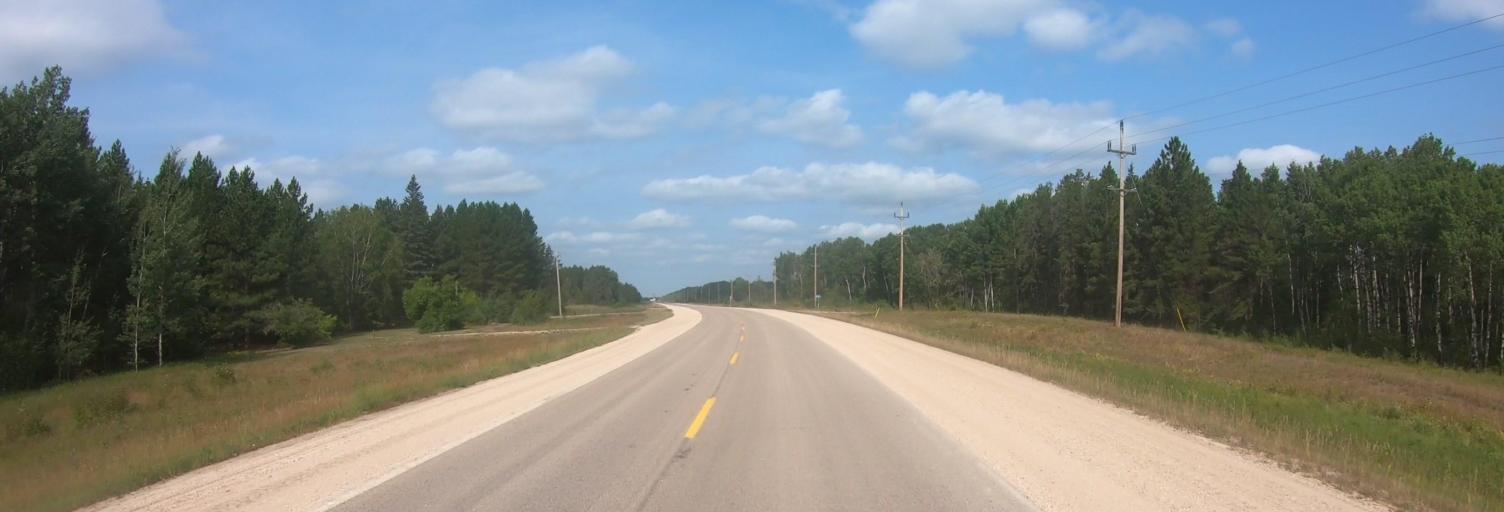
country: CA
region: Manitoba
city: La Broquerie
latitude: 49.2188
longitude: -96.3033
